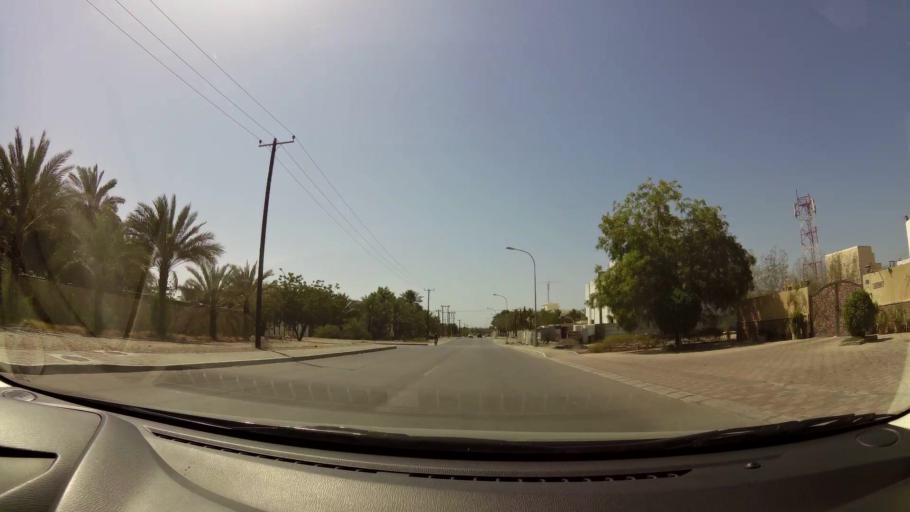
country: OM
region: Muhafazat Masqat
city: As Sib al Jadidah
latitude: 23.6313
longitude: 58.2216
